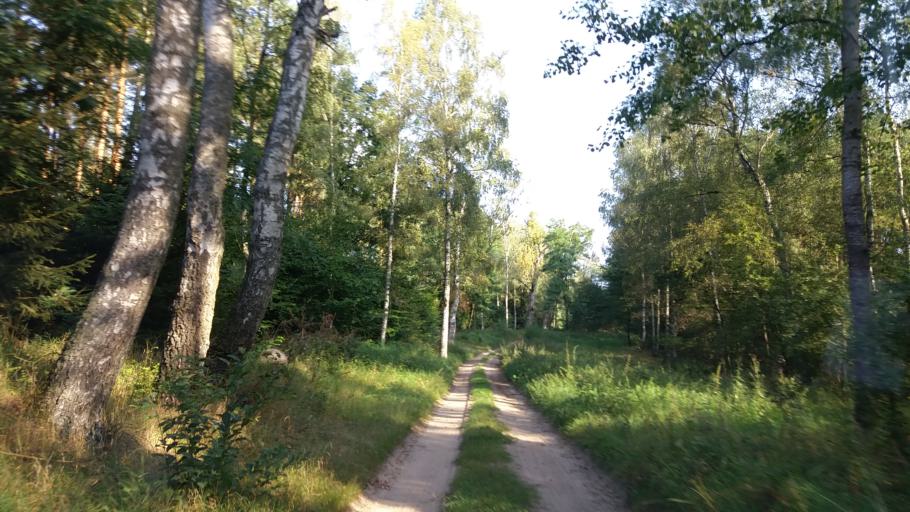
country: PL
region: West Pomeranian Voivodeship
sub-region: Powiat choszczenski
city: Recz
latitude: 53.2019
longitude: 15.5416
